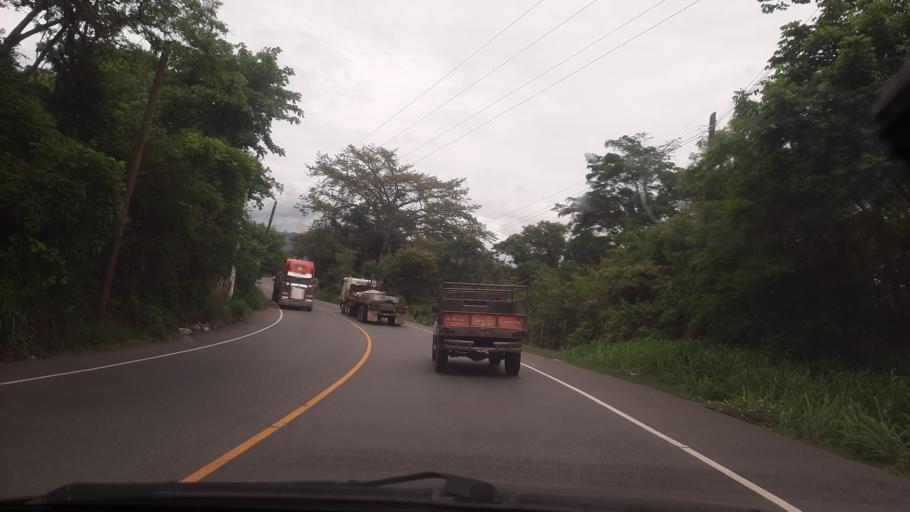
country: GT
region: Zacapa
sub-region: Municipio de Zacapa
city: Gualan
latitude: 15.1380
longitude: -89.3393
